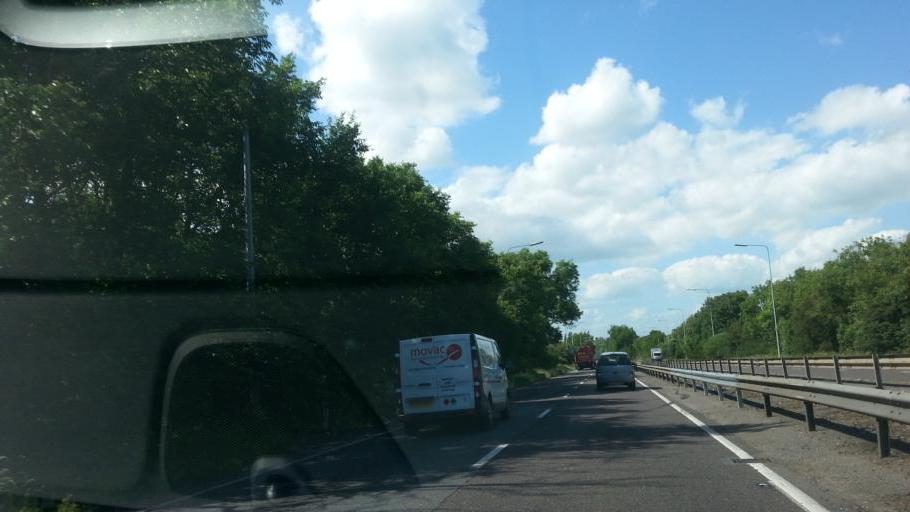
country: GB
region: England
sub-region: Central Bedfordshire
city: Astwick
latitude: 52.0354
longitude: -0.2187
